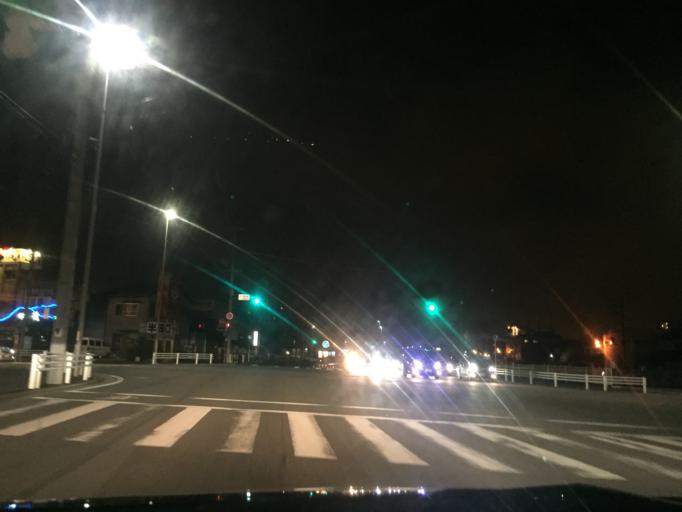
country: JP
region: Aichi
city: Handa
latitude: 34.8804
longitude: 136.9195
